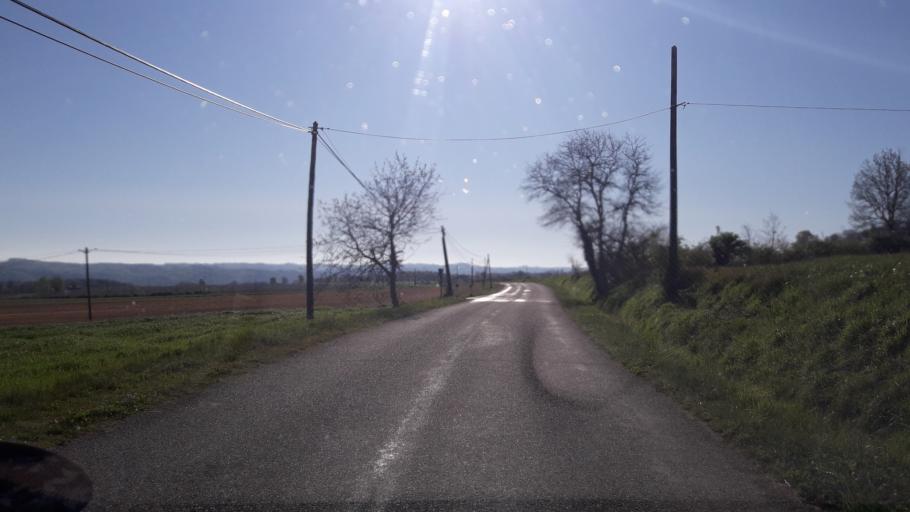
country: FR
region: Midi-Pyrenees
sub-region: Departement de la Haute-Garonne
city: Montesquieu-Volvestre
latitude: 43.2010
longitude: 1.1847
